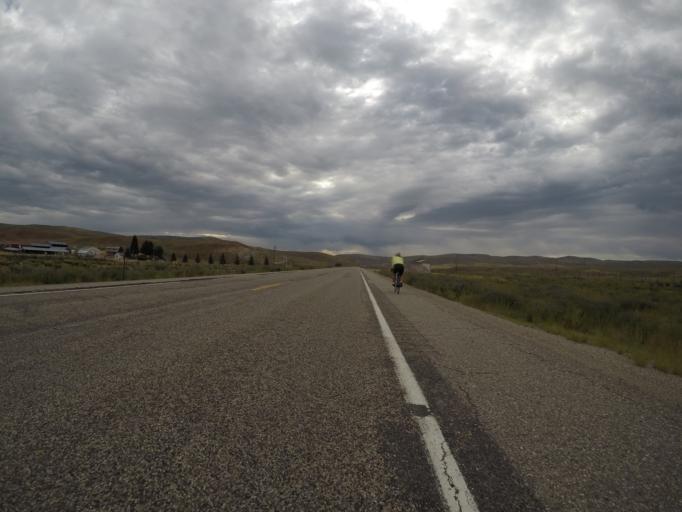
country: US
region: Utah
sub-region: Rich County
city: Randolph
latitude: 41.8247
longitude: -110.9098
